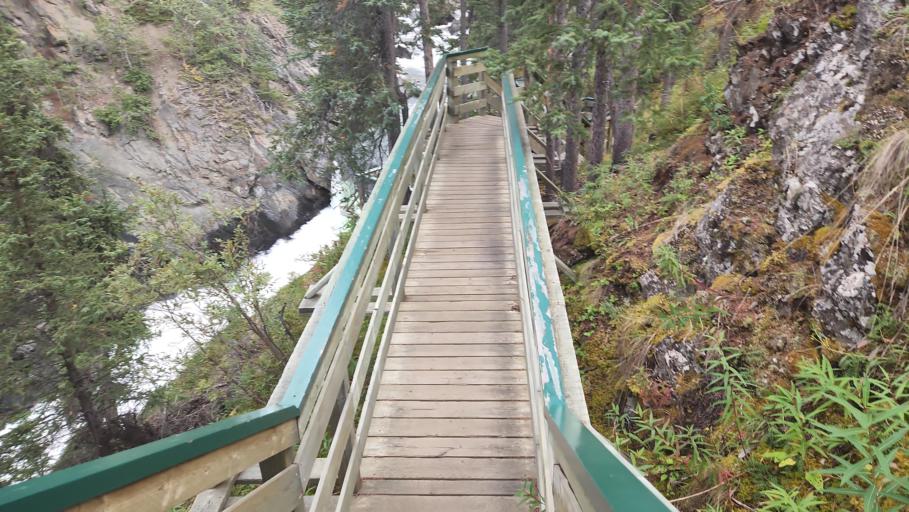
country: CA
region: Yukon
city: Haines Junction
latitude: 60.1082
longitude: -136.9468
